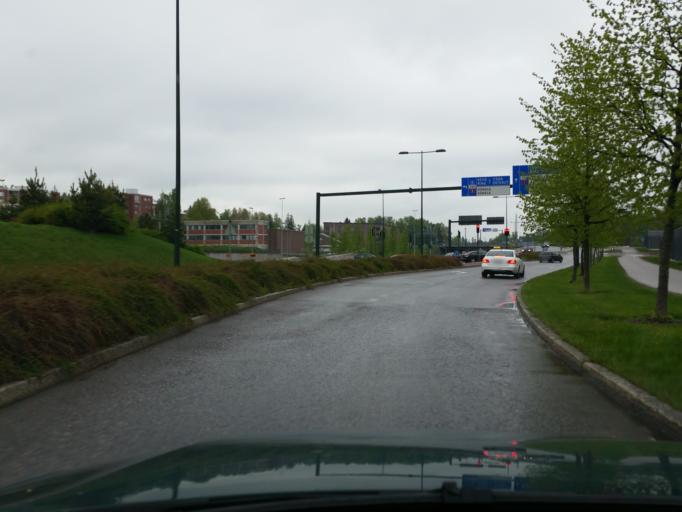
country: FI
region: Uusimaa
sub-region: Helsinki
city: Teekkarikylae
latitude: 60.2246
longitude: 24.8259
